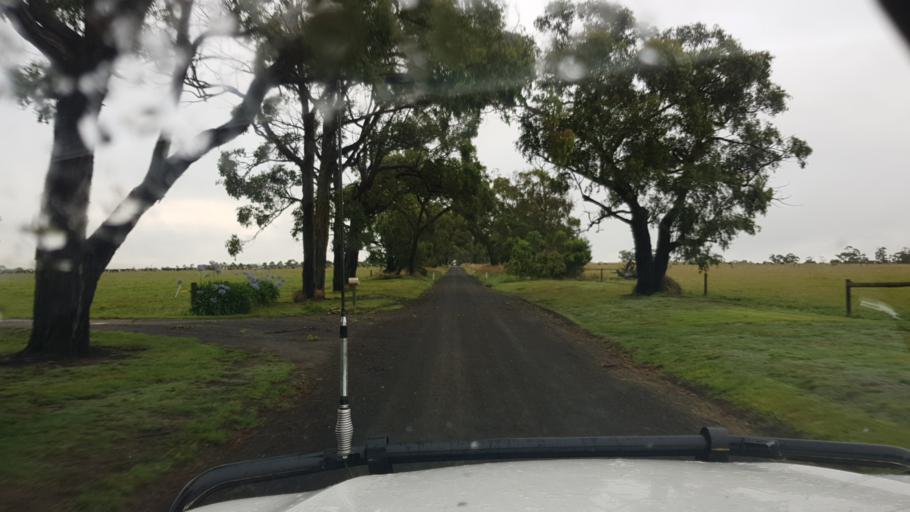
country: AU
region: Victoria
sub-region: Latrobe
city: Moe
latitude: -38.1616
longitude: 146.1610
